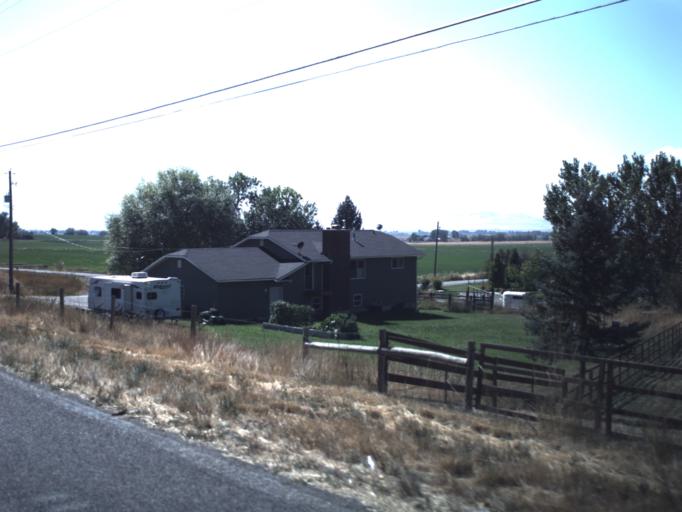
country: US
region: Utah
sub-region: Cache County
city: Richmond
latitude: 41.8802
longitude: -111.8216
